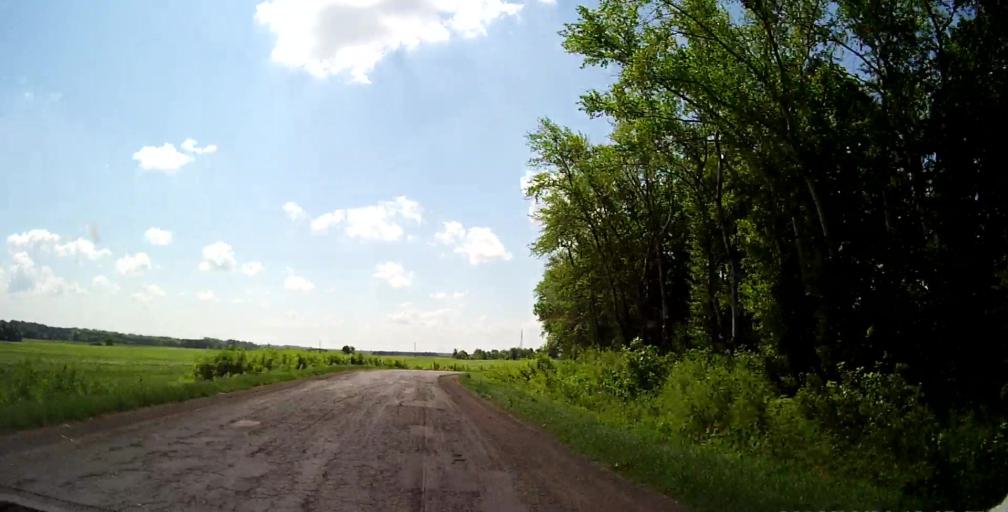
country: RU
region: Lipetsk
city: Chaplygin
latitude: 53.2974
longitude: 39.9547
